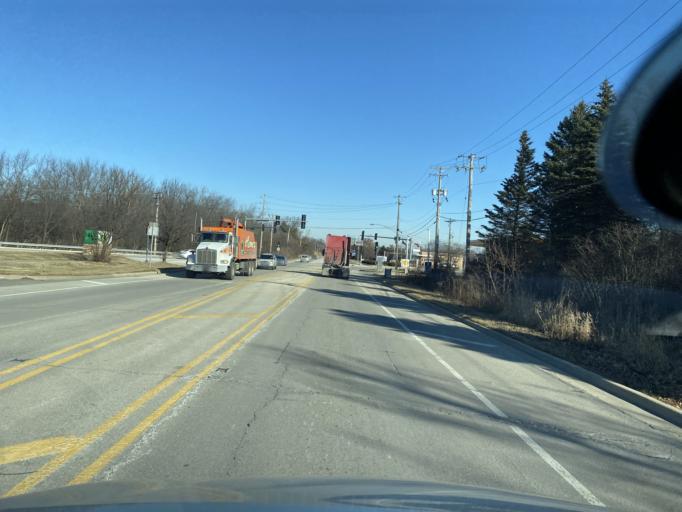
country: US
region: Illinois
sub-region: Cook County
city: Lemont
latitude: 41.6641
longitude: -87.9625
